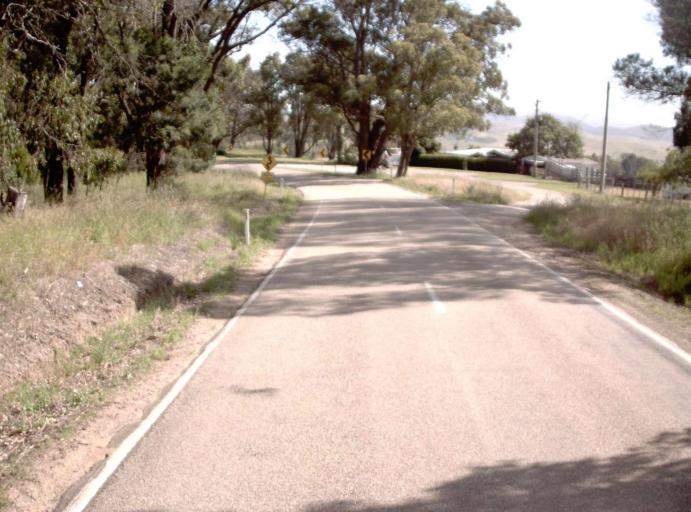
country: AU
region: Victoria
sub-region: East Gippsland
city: Lakes Entrance
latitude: -37.5218
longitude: 148.1622
